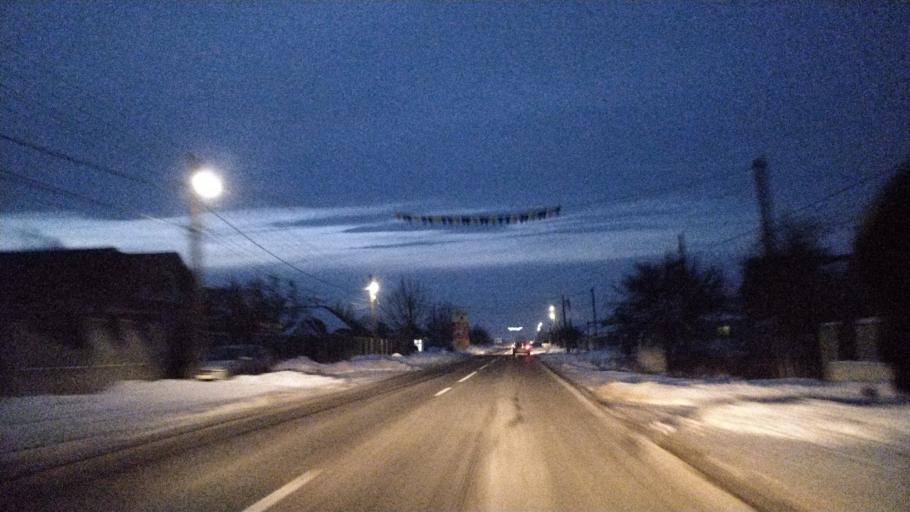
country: RO
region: Vrancea
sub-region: Comuna Rastoaca
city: Rastoaca
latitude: 45.6664
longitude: 27.2686
